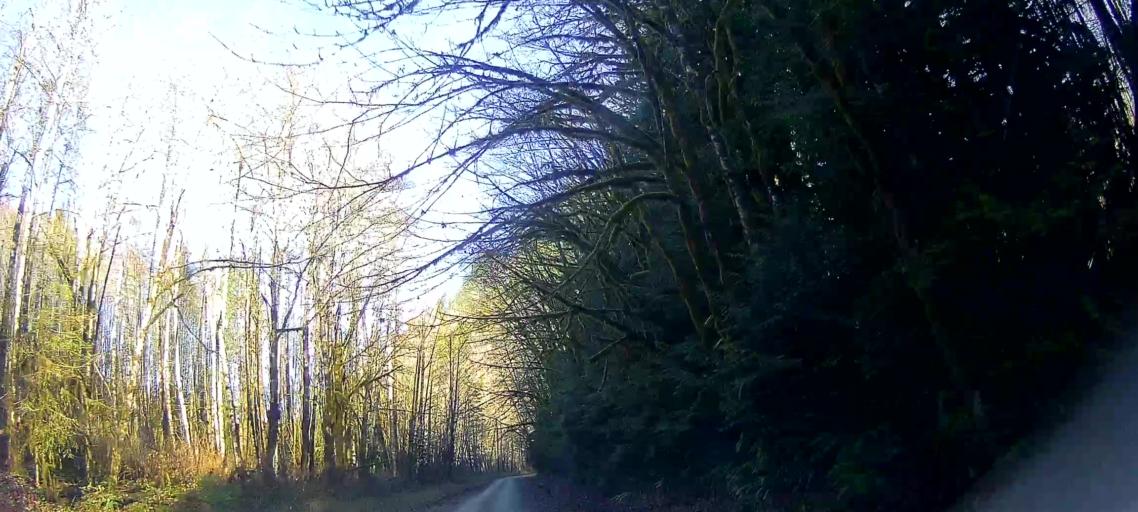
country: US
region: Washington
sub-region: Snohomish County
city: Darrington
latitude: 48.5482
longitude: -121.7282
